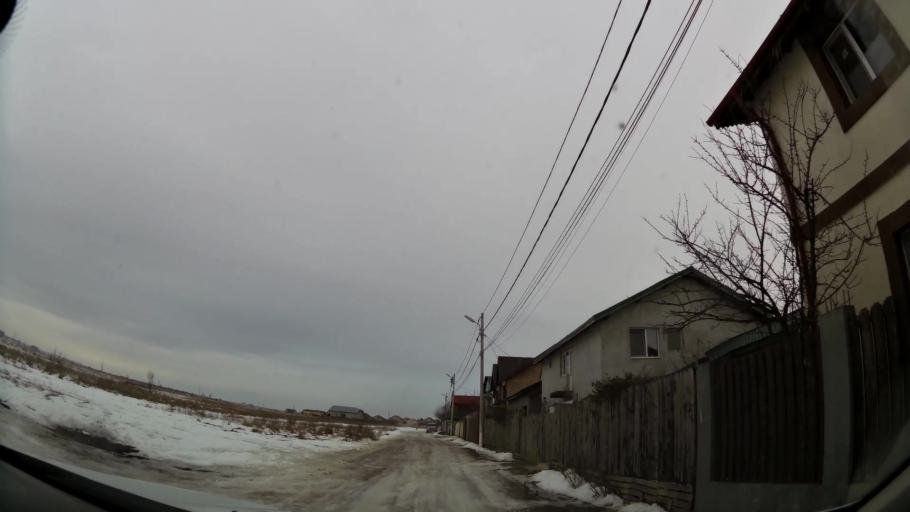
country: RO
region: Ilfov
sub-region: Comuna Pantelimon
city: Pantelimon
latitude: 44.4645
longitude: 26.2042
